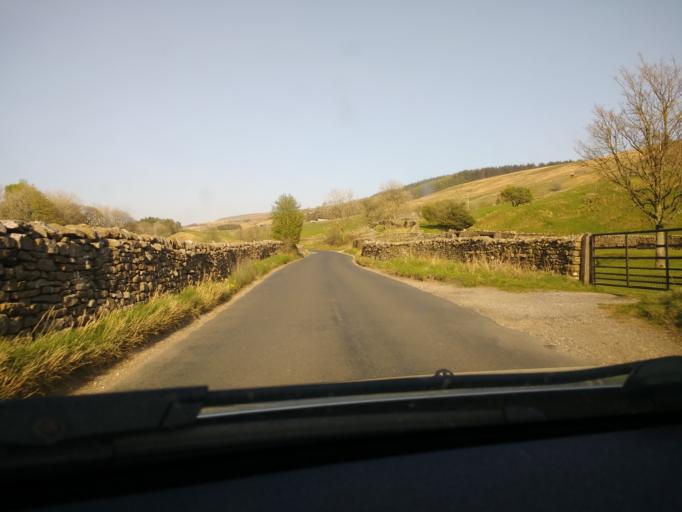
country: GB
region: England
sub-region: Cumbria
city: Sedbergh
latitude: 54.3042
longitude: -2.3712
